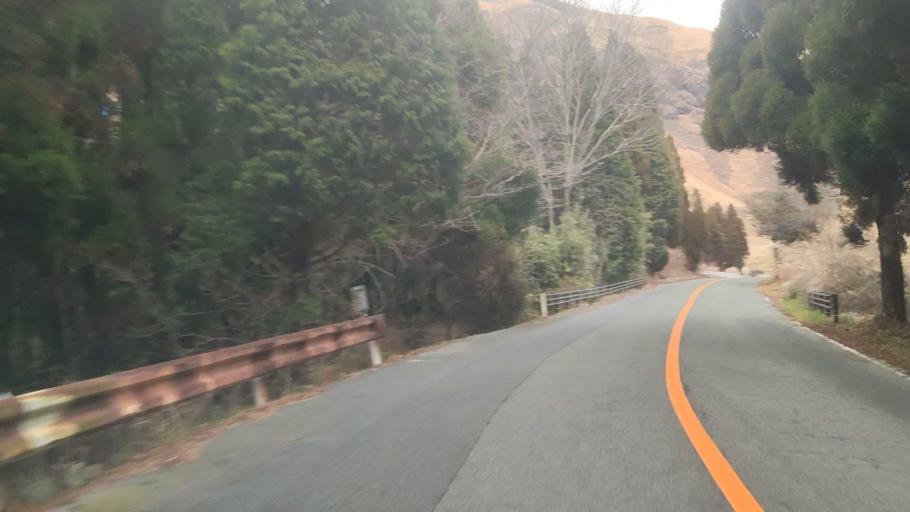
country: JP
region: Kumamoto
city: Aso
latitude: 32.9085
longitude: 131.1431
